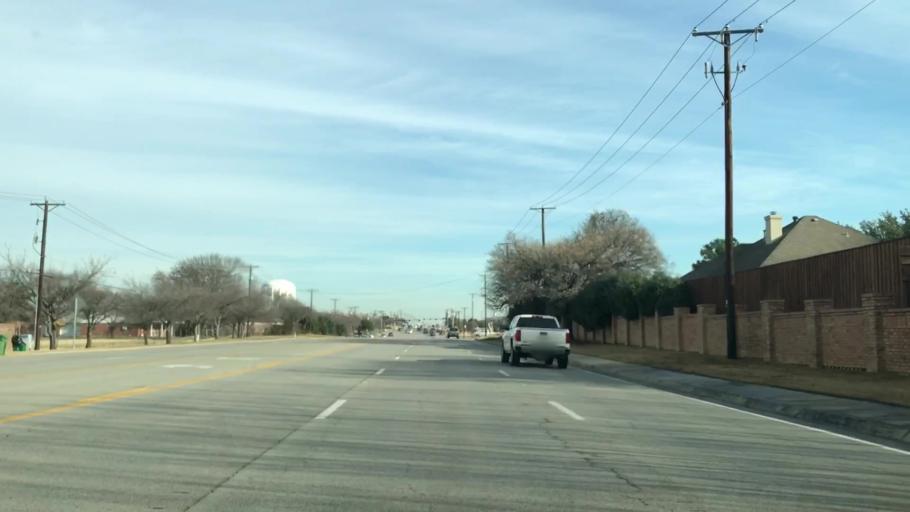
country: US
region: Texas
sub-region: Tarrant County
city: Colleyville
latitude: 32.8998
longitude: -97.1965
